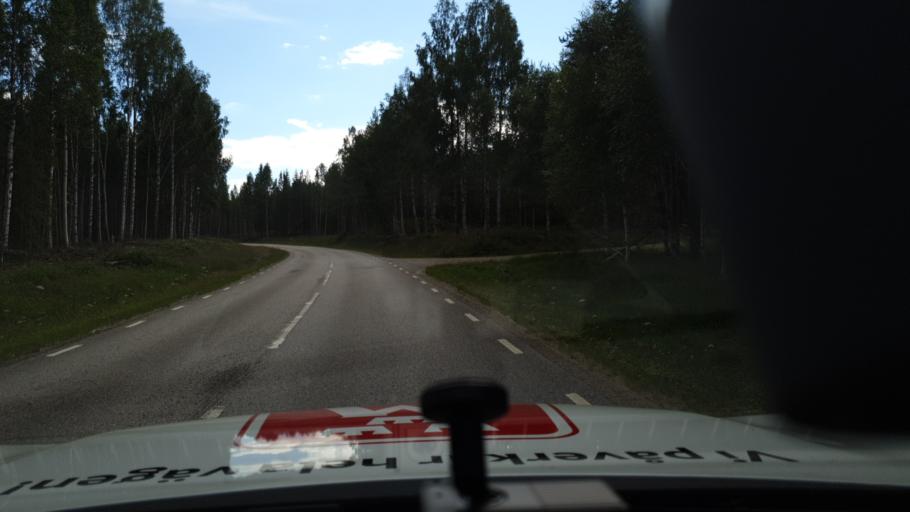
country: NO
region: Hedmark
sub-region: Trysil
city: Innbygda
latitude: 61.0280
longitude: 12.4681
